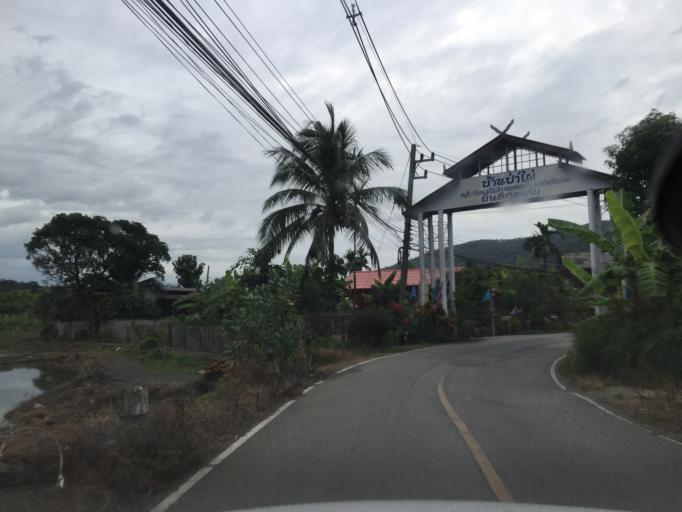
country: TH
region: Chiang Mai
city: Mae On
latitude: 18.8312
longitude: 99.1842
